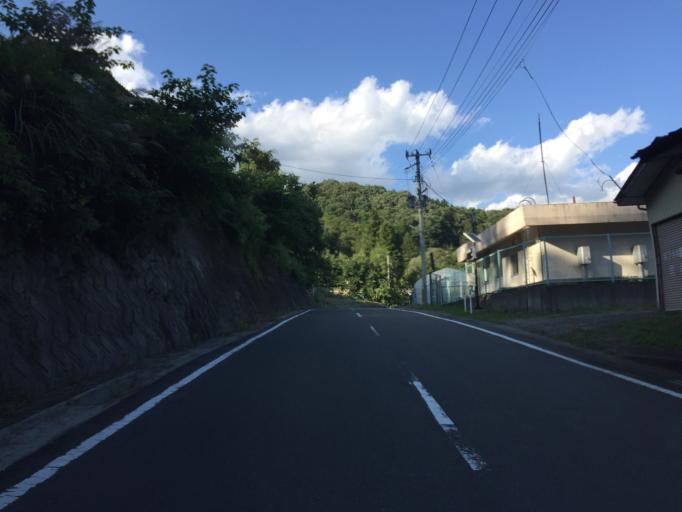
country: JP
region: Fukushima
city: Fukushima-shi
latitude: 37.7201
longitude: 140.5148
